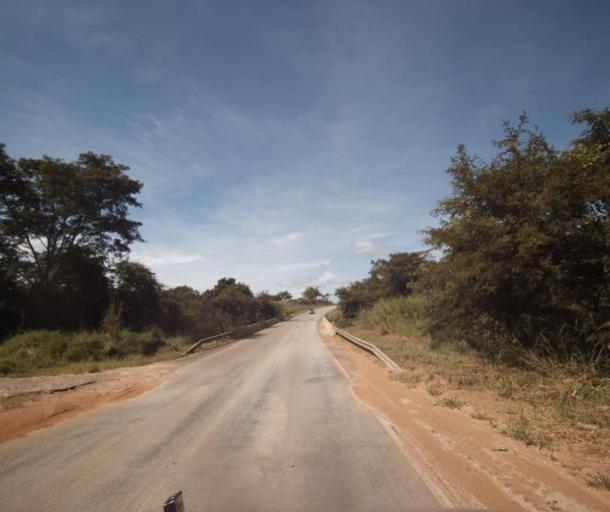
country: BR
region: Goias
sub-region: Abadiania
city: Abadiania
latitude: -16.1373
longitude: -48.8917
